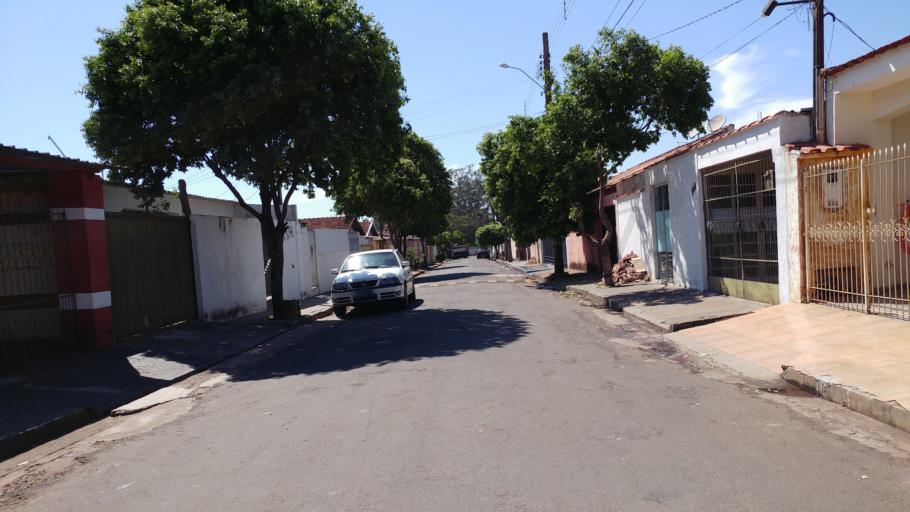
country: BR
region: Sao Paulo
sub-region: Paraguacu Paulista
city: Paraguacu Paulista
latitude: -22.4277
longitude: -50.5801
